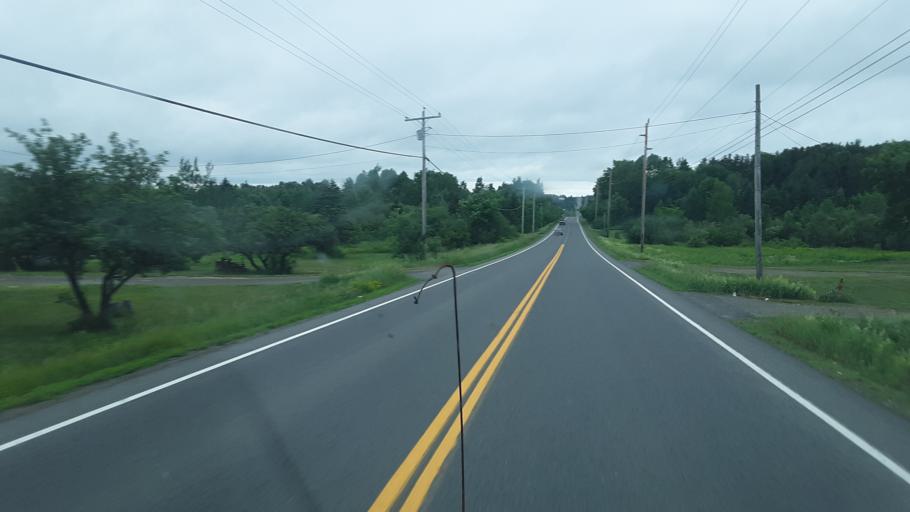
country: US
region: Maine
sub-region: Penobscot County
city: Patten
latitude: 45.9783
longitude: -68.4502
